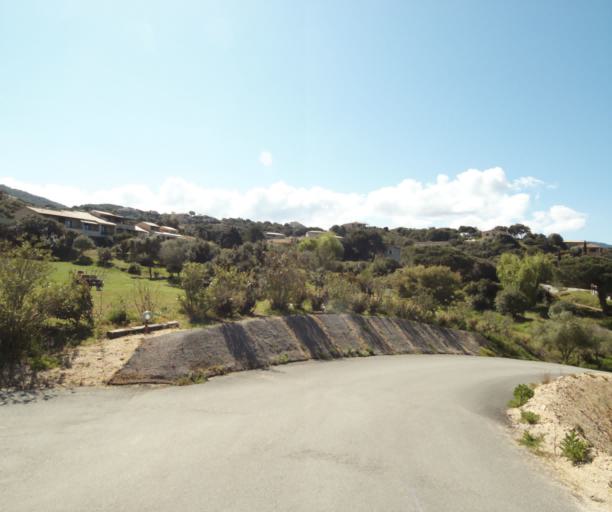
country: FR
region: Corsica
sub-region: Departement de la Corse-du-Sud
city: Propriano
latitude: 41.6794
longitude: 8.9166
